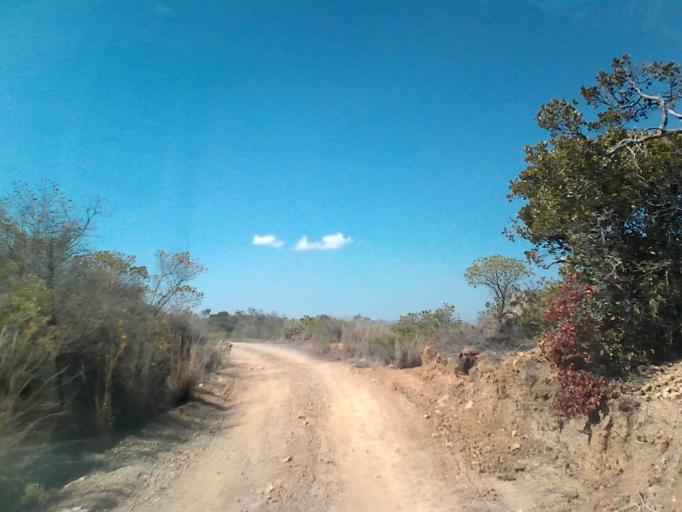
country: CO
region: Boyaca
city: Sachica
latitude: 5.5556
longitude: -73.5656
